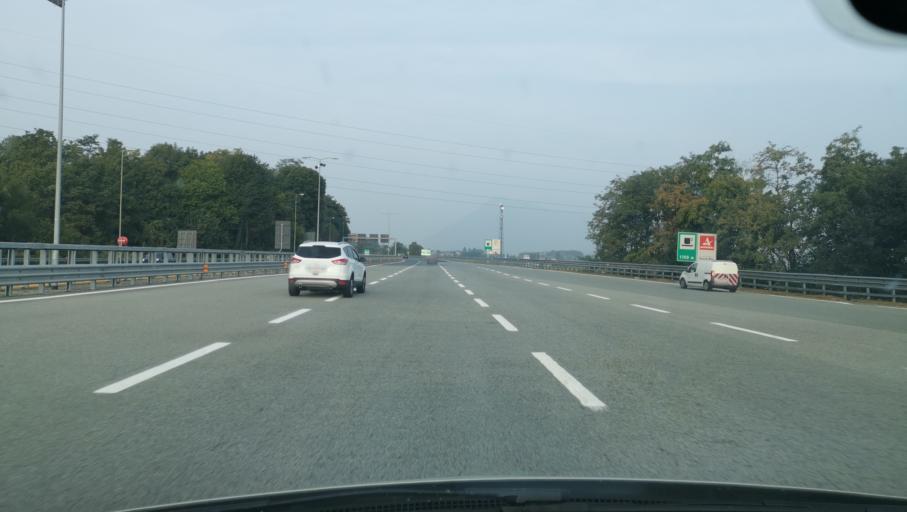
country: IT
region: Piedmont
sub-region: Provincia di Torino
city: Rivoli
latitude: 45.0828
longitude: 7.5394
